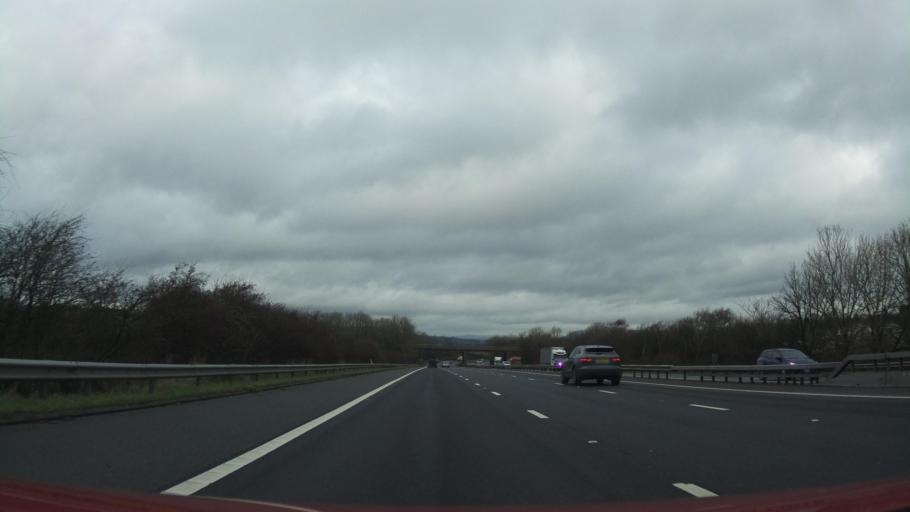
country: GB
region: England
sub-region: Lancashire
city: Carnforth
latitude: 54.1034
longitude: -2.7663
